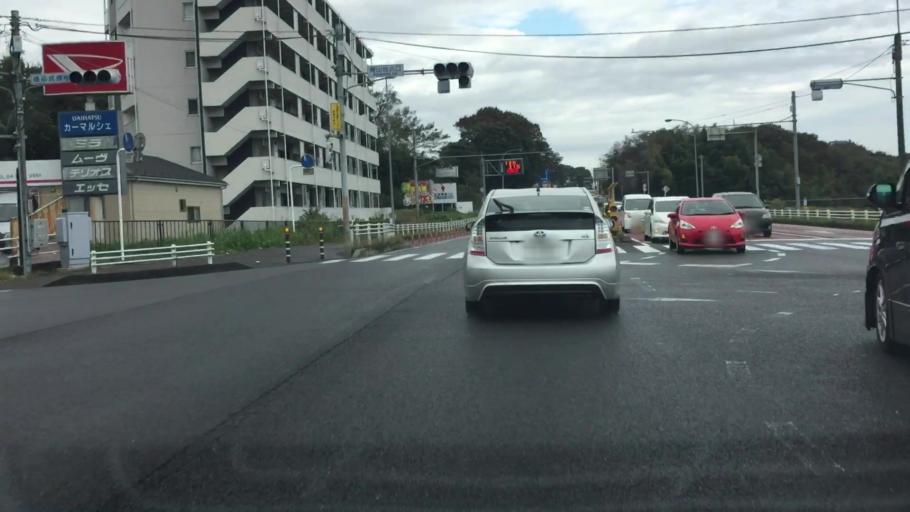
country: JP
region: Chiba
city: Abiko
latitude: 35.8812
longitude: 140.0433
